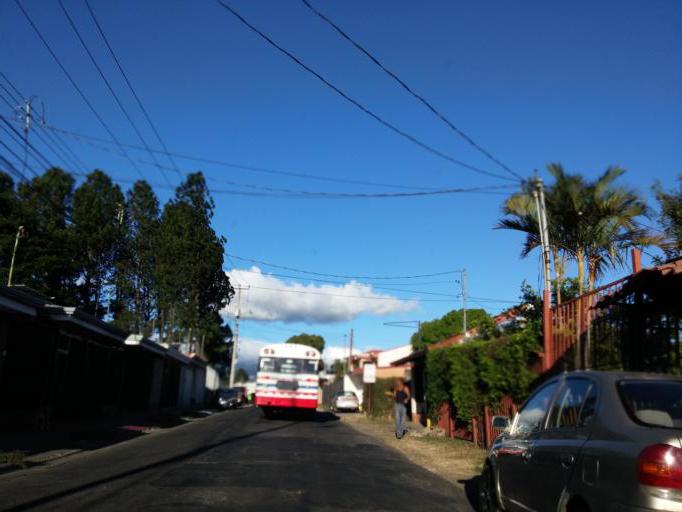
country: CR
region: Alajuela
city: Alajuela
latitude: 10.0159
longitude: -84.1977
